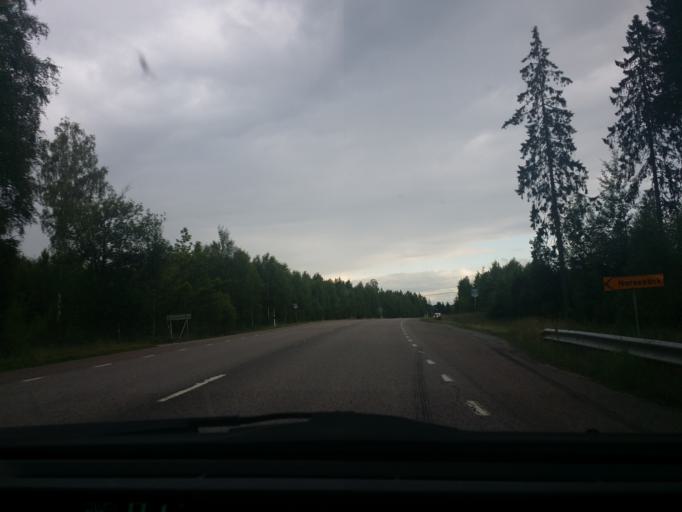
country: SE
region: OErebro
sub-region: Orebro Kommun
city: Hovsta
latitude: 59.4349
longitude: 15.1613
